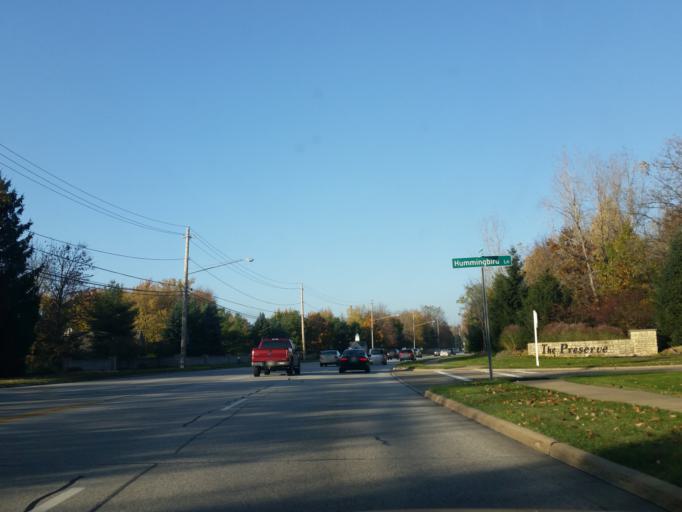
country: US
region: Ohio
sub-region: Cuyahoga County
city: North Olmsted
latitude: 41.4334
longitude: -81.9493
